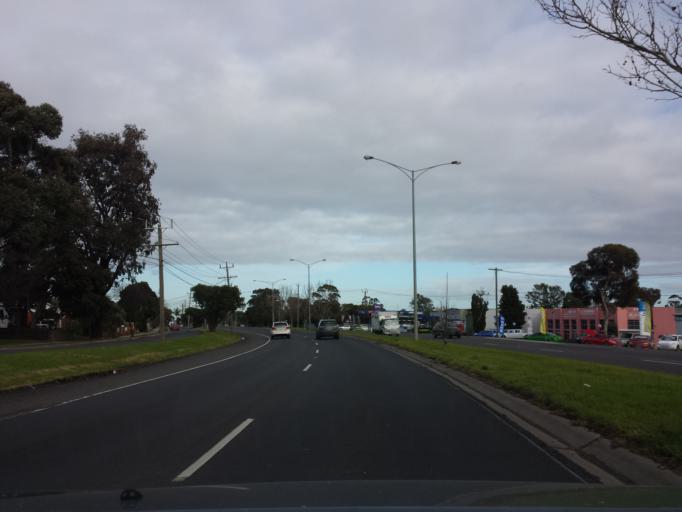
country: AU
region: Victoria
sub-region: Knox
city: Knoxfield
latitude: -37.8840
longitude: 145.2701
